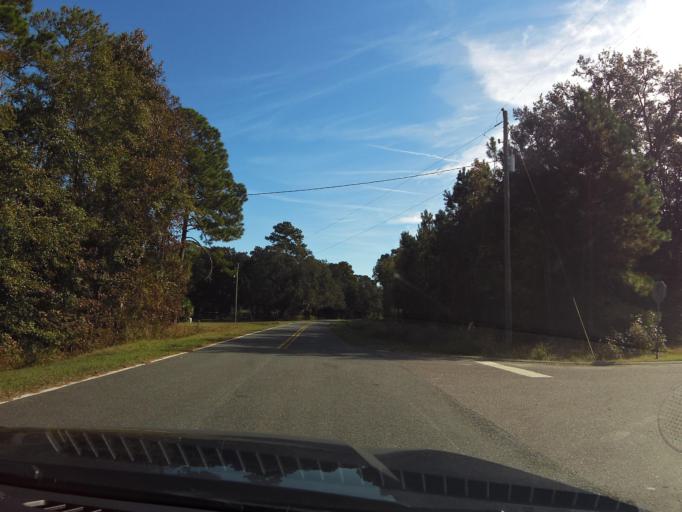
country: US
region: Georgia
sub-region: Glynn County
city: Brunswick
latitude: 31.1413
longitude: -81.5707
